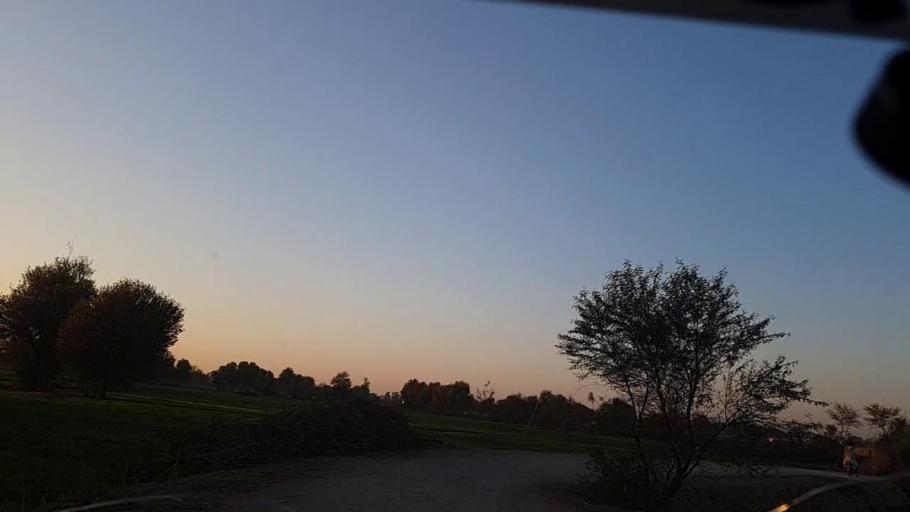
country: PK
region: Sindh
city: Adilpur
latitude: 27.8391
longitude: 69.2985
